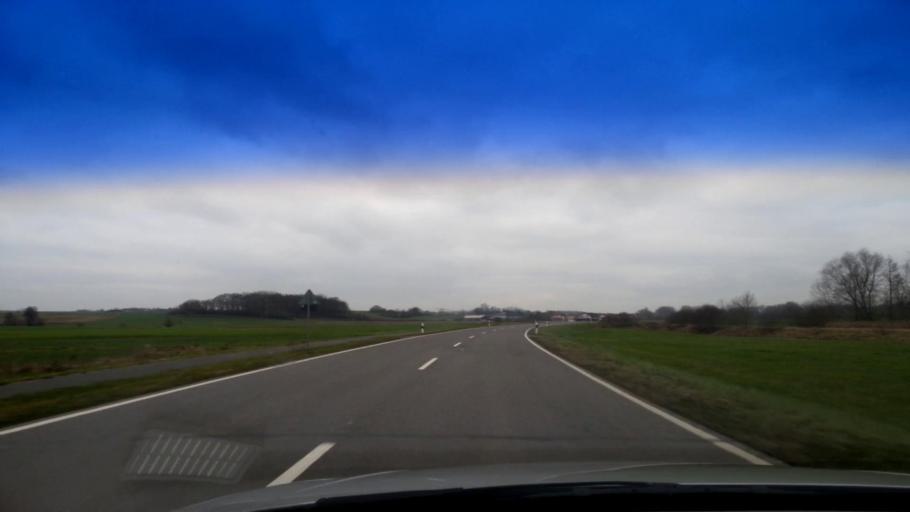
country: DE
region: Bavaria
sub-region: Upper Franconia
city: Walsdorf
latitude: 49.8189
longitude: 10.7953
